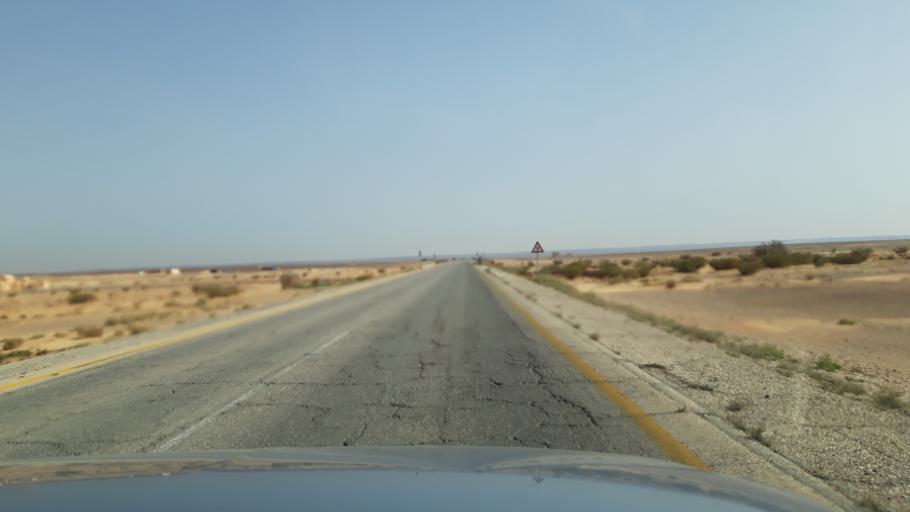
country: JO
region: Amman
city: Al Azraq ash Shamali
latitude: 31.7984
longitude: 36.5876
